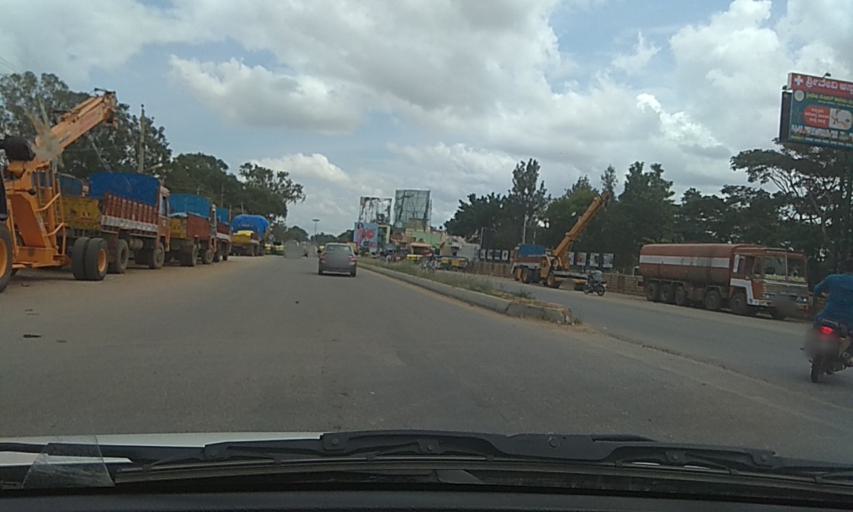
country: IN
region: Karnataka
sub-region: Tumkur
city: Tumkur
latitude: 13.3772
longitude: 77.0988
